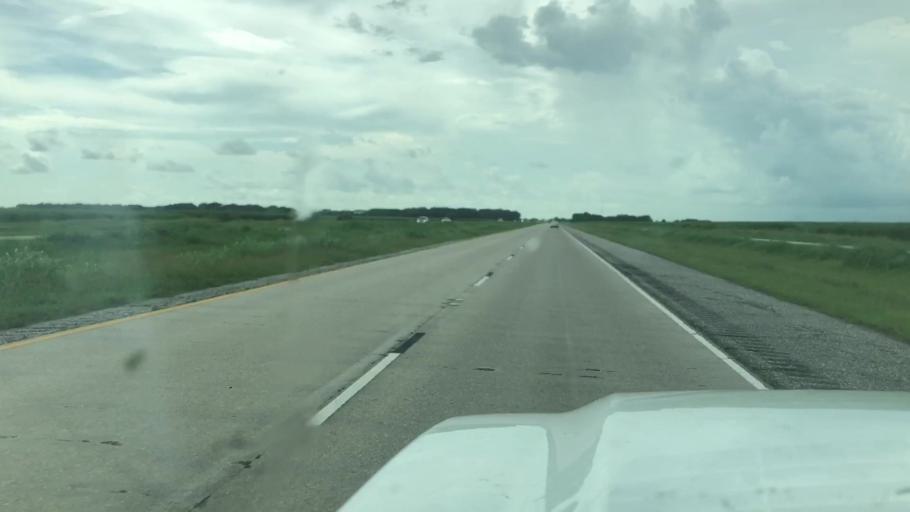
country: US
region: Louisiana
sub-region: Saint Mary Parish
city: Baldwin
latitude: 29.8503
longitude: -91.5964
